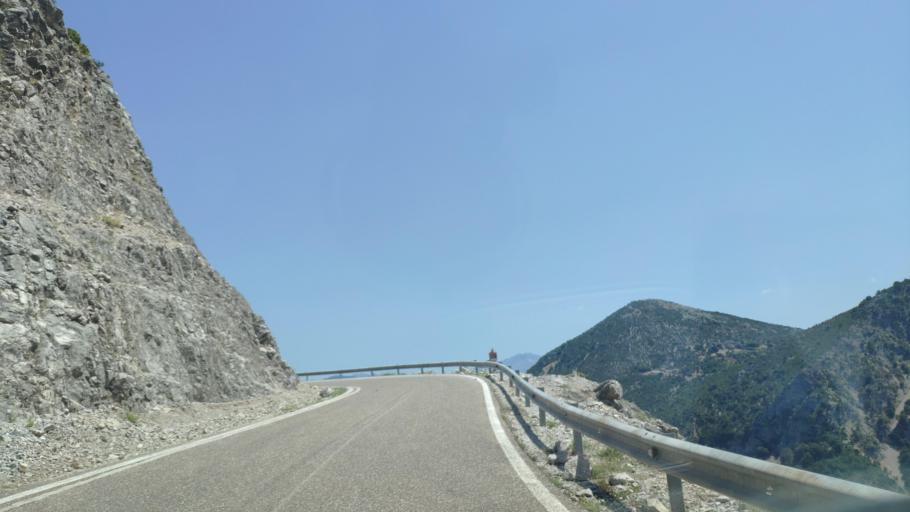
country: GR
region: West Greece
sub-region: Nomos Aitolias kai Akarnanias
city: Krikellos
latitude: 39.0190
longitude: 21.3690
